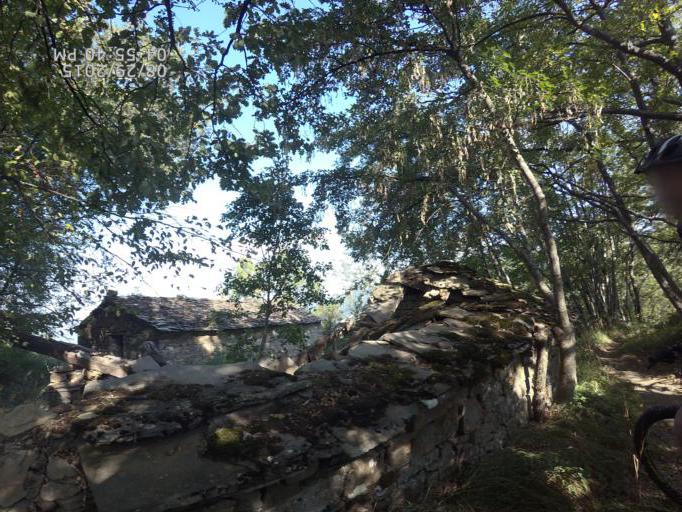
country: IT
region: Emilia-Romagna
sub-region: Provincia di Modena
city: Sestola
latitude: 44.2033
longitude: 10.7694
